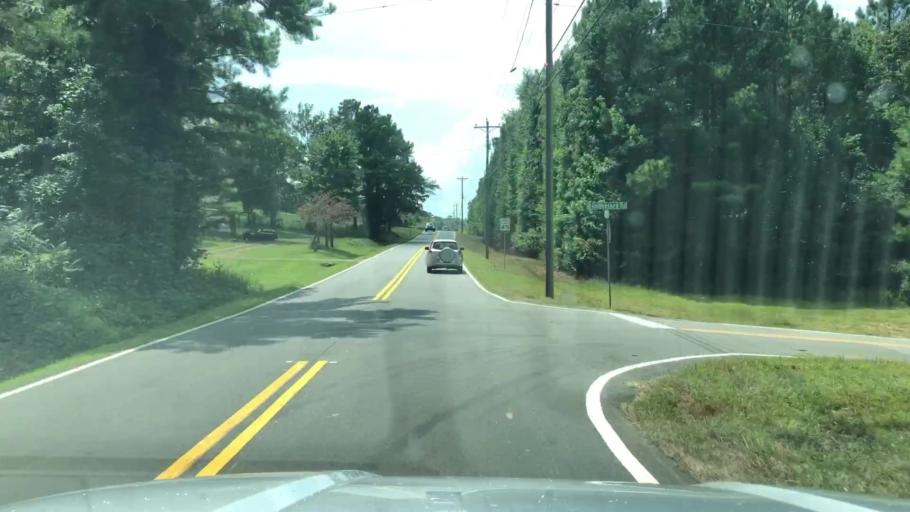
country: US
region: Georgia
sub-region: Bartow County
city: Emerson
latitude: 34.0569
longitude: -84.8162
